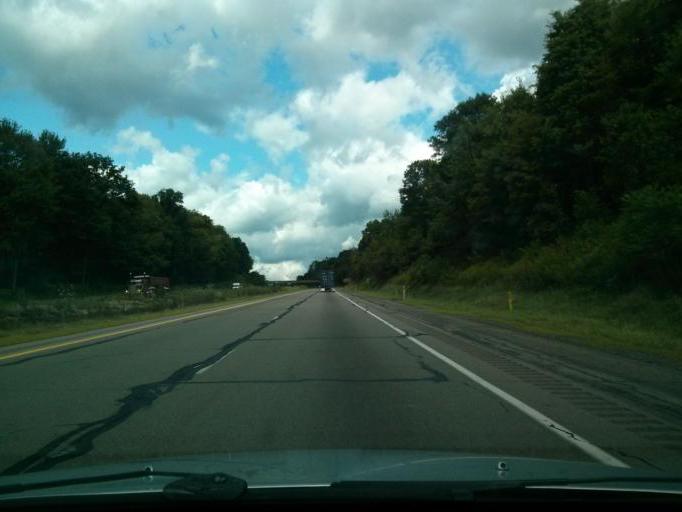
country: US
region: Pennsylvania
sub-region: Jefferson County
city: Brookville
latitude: 41.1661
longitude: -79.0080
